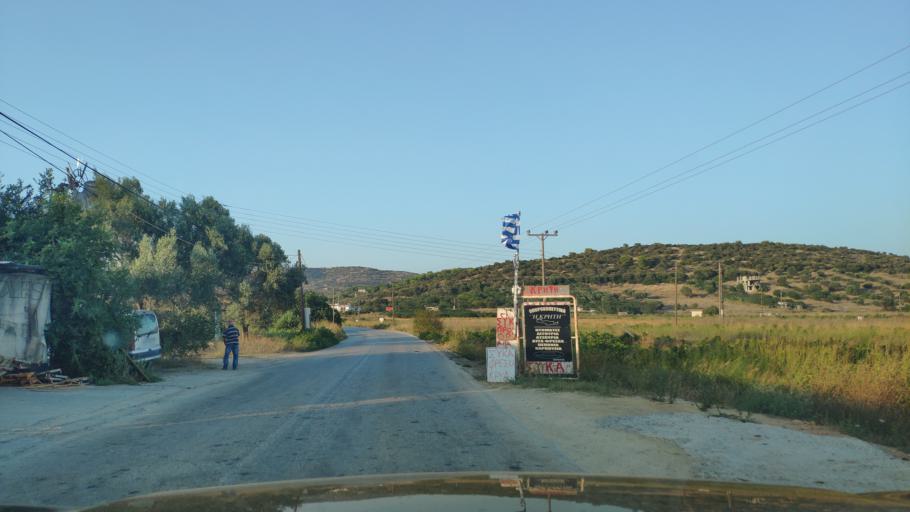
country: GR
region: Attica
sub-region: Nomarchia Anatolikis Attikis
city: Limin Mesoyaias
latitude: 37.9254
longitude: 23.9787
